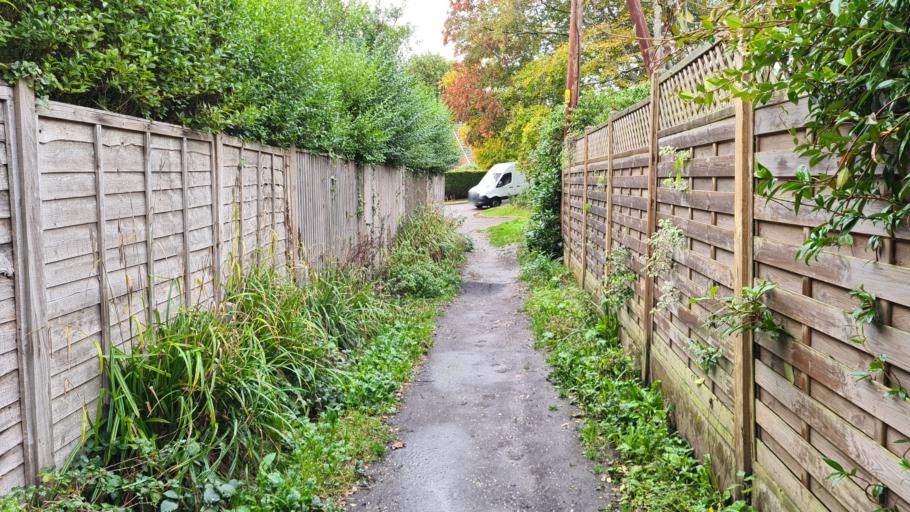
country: GB
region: England
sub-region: West Sussex
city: Storrington
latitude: 50.9213
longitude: -0.4346
